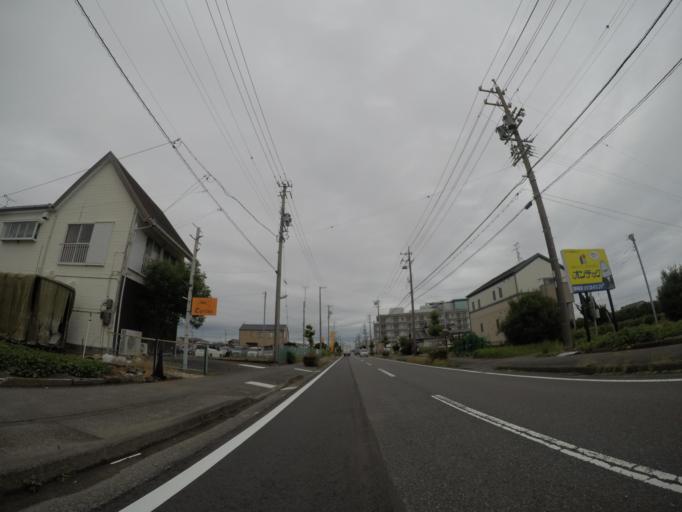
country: JP
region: Shizuoka
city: Sagara
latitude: 34.7547
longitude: 138.2359
